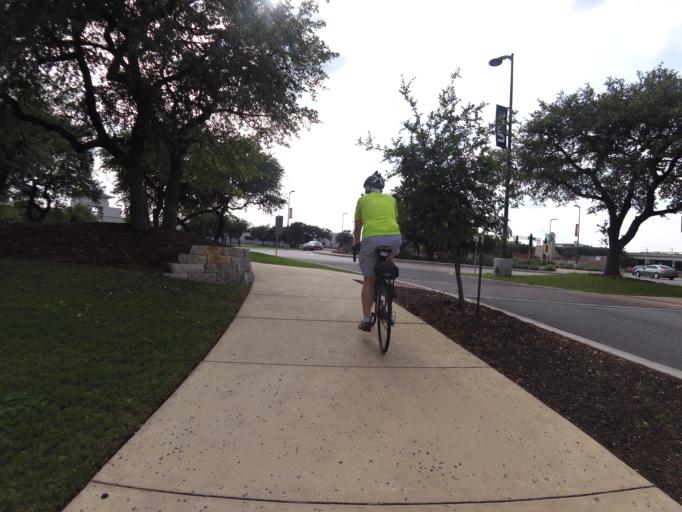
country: US
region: Texas
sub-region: Bexar County
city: Shavano Park
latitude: 29.5869
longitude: -98.6190
